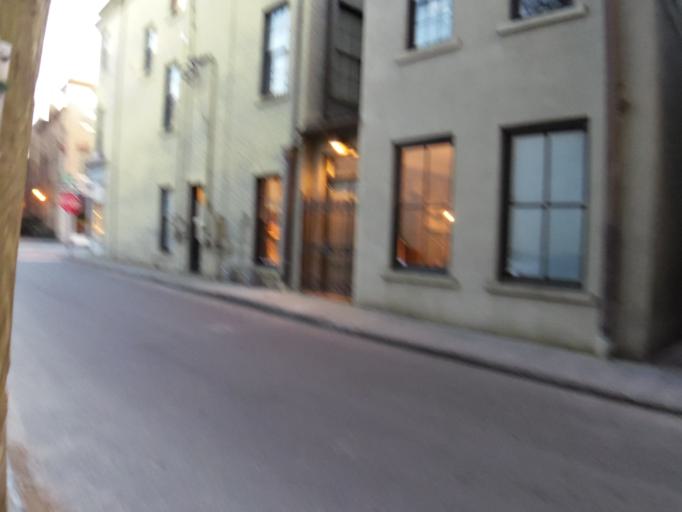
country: US
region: South Carolina
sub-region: Charleston County
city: Charleston
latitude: 32.7797
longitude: -79.9335
